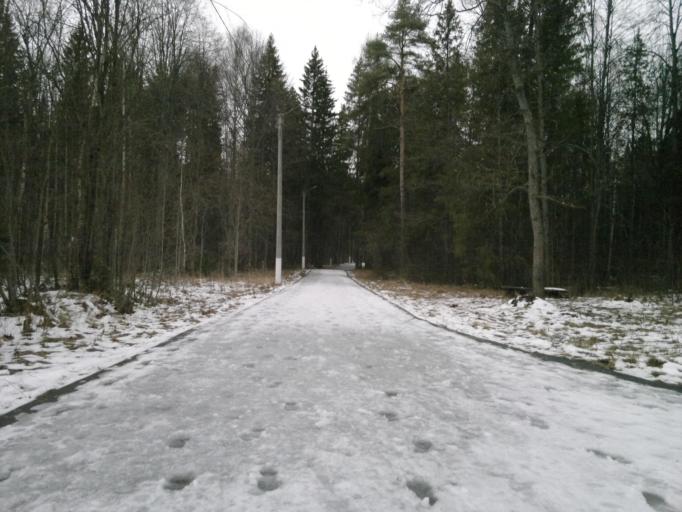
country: RU
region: Mariy-El
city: Yoshkar-Ola
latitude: 56.6005
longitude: 47.9662
